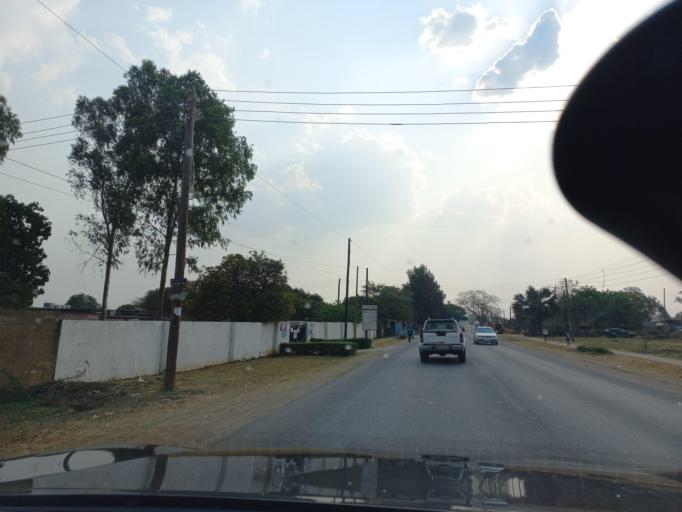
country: ZM
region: Lusaka
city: Lusaka
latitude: -15.4637
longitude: 28.2413
